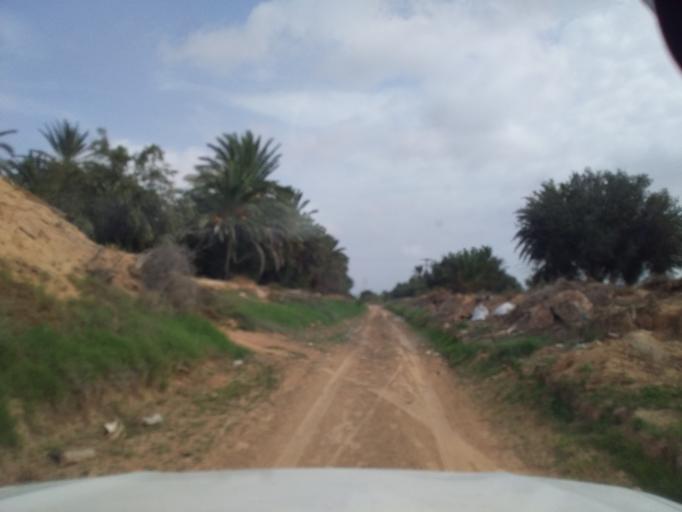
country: TN
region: Qabis
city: Gabes
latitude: 33.6316
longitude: 10.3025
